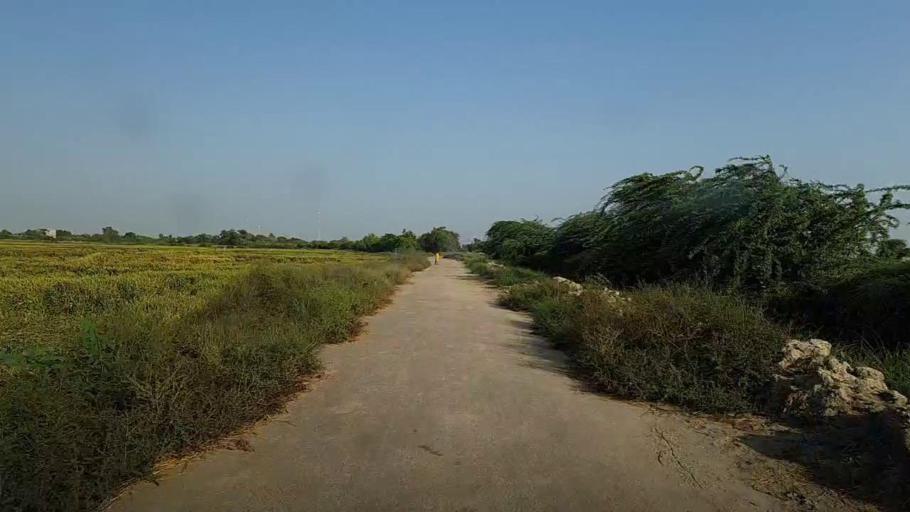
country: PK
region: Sindh
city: Bulri
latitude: 24.7572
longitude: 68.4052
